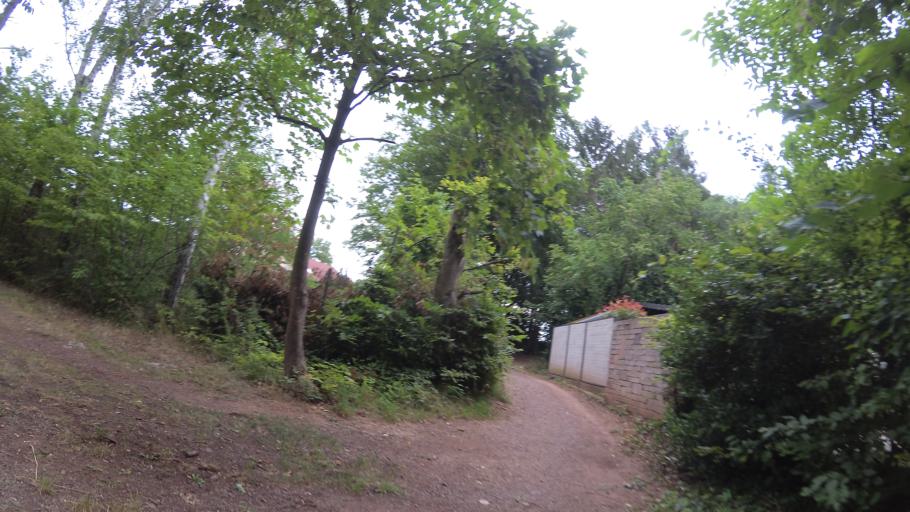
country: DE
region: Saarland
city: Schwalbach
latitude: 49.3112
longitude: 6.8129
